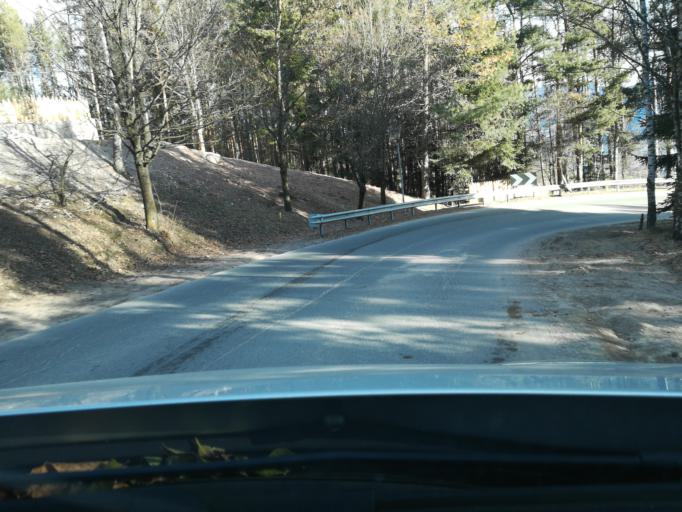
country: IT
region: Trentino-Alto Adige
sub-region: Bolzano
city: Renon - Ritten
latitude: 46.5456
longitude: 11.4594
